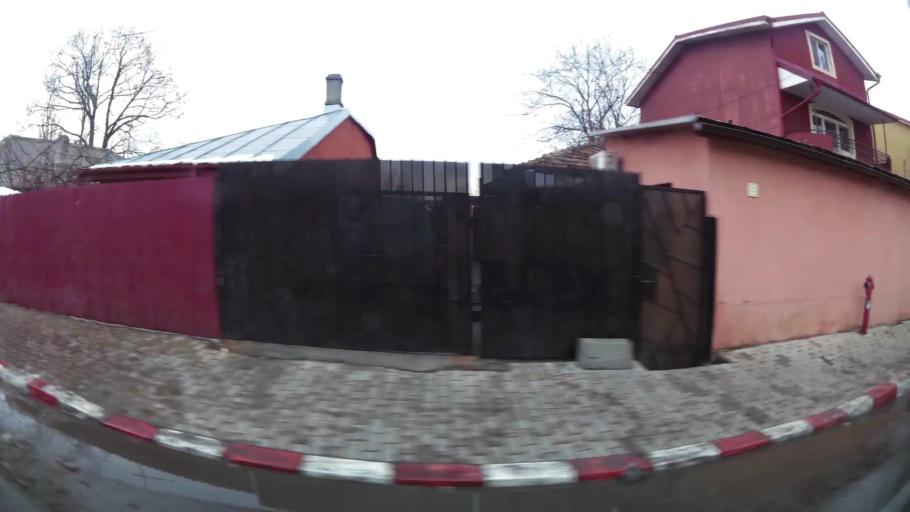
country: RO
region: Ilfov
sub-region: Voluntari City
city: Voluntari
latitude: 44.4838
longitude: 26.1695
